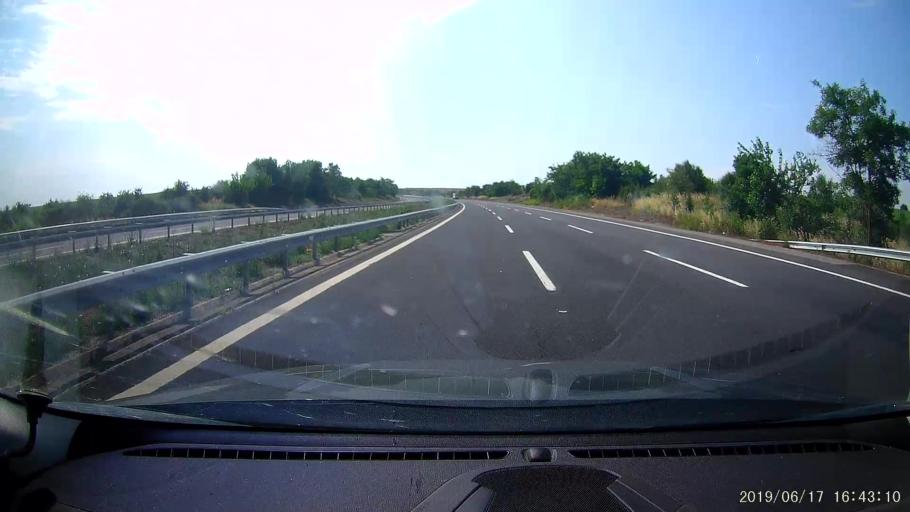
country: TR
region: Kirklareli
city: Luleburgaz
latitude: 41.4793
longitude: 27.3015
